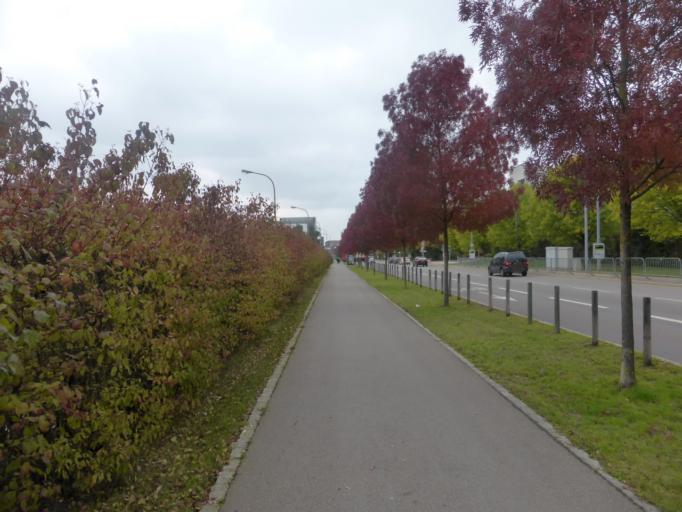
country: LU
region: Luxembourg
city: Kirchberg
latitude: 49.6371
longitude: 6.1711
